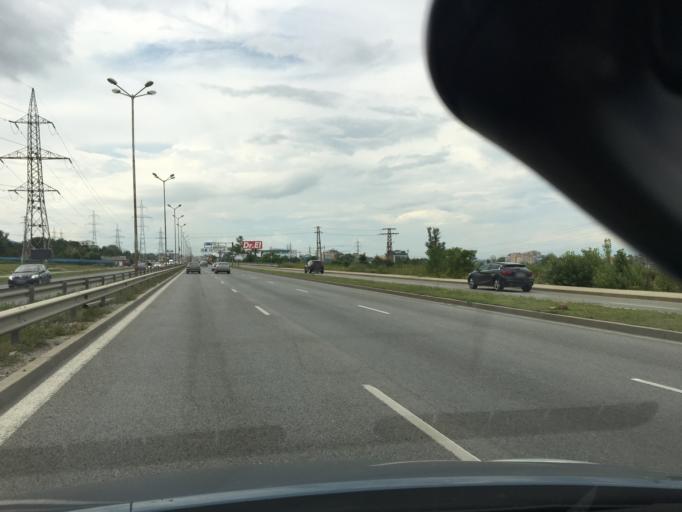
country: BG
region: Sofia-Capital
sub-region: Stolichna Obshtina
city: Sofia
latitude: 42.6295
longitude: 23.3425
